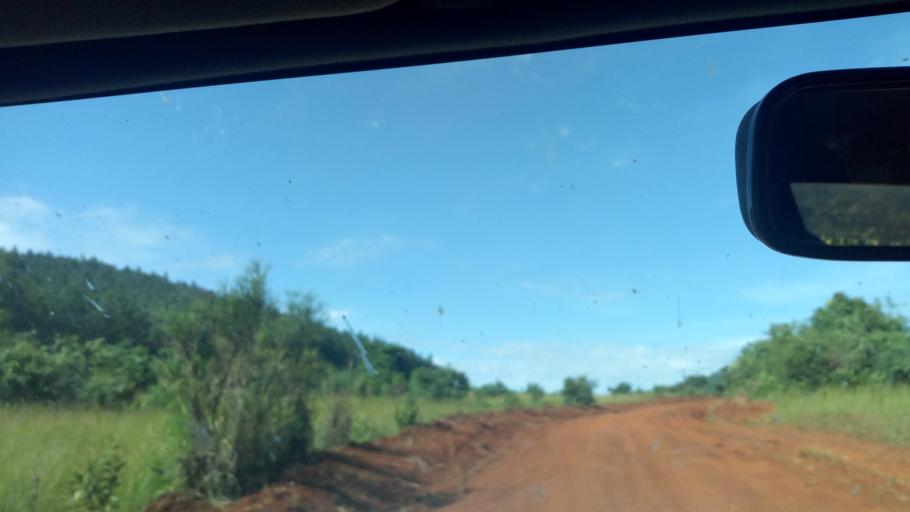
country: UG
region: Western Region
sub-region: Masindi District
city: Masindi
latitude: 1.6468
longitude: 31.7757
